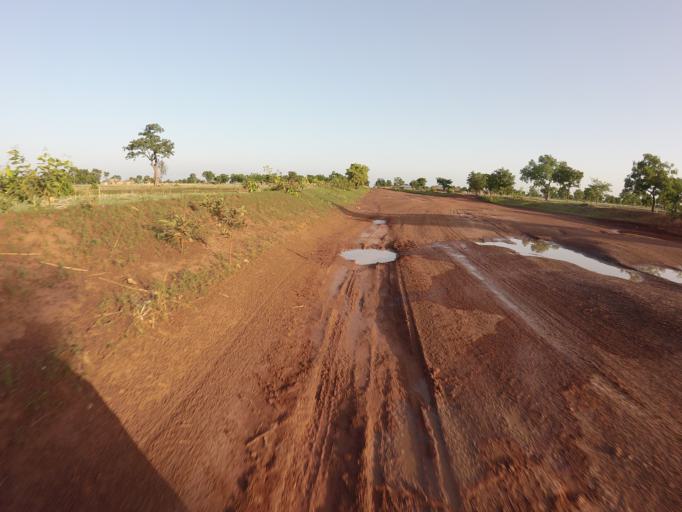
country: TG
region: Savanes
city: Sansanne-Mango
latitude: 10.2690
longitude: -0.0813
